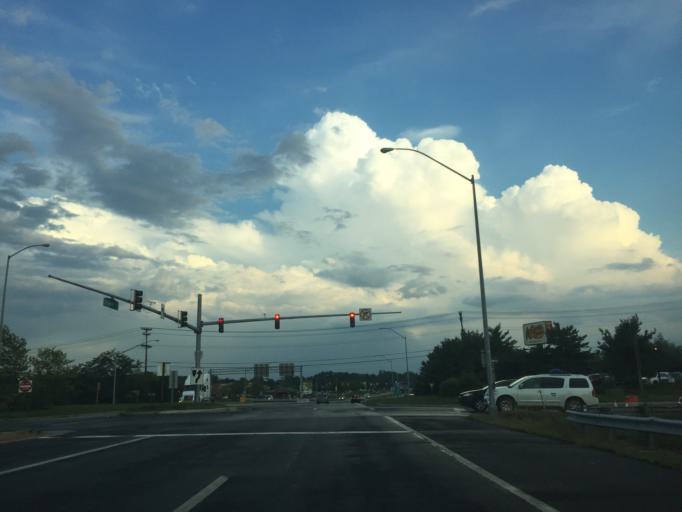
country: US
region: Maryland
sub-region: Harford County
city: Riverside
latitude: 39.4832
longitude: -76.2509
